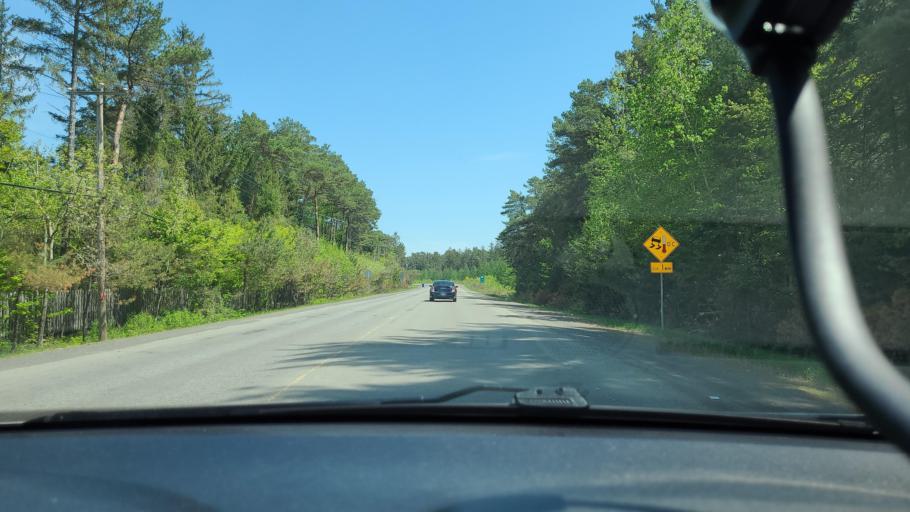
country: CA
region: Quebec
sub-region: Laurentides
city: Lachute
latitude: 45.6642
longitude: -74.2568
